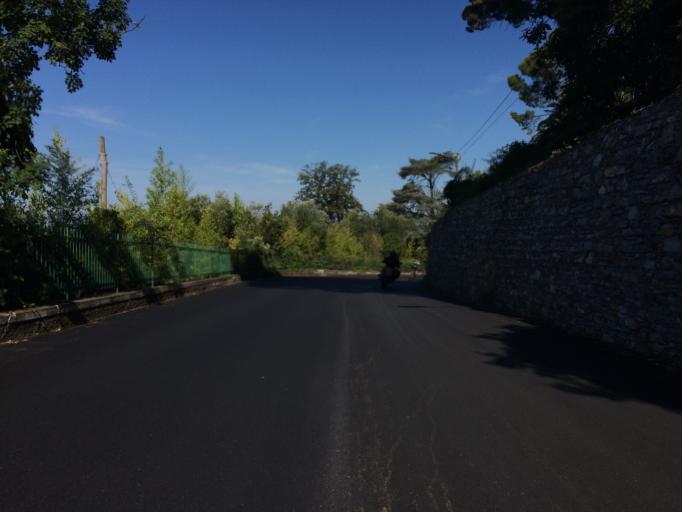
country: IT
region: Liguria
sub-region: Provincia di Genova
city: Camogli
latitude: 44.3486
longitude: 9.1634
